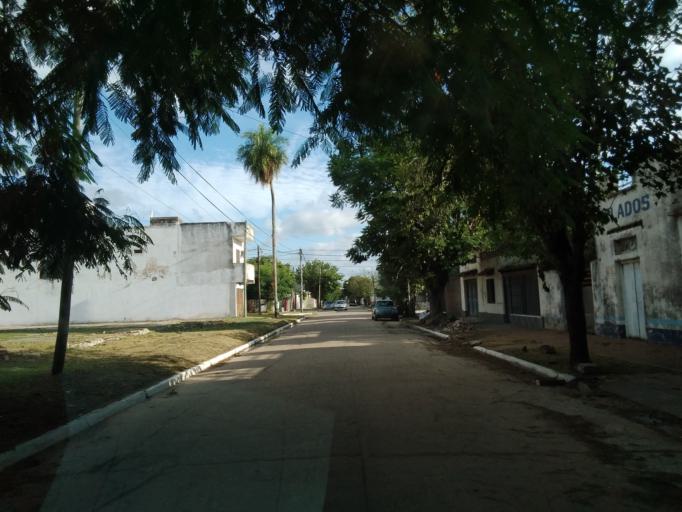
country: AR
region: Corrientes
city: Corrientes
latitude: -27.4579
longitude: -58.8189
